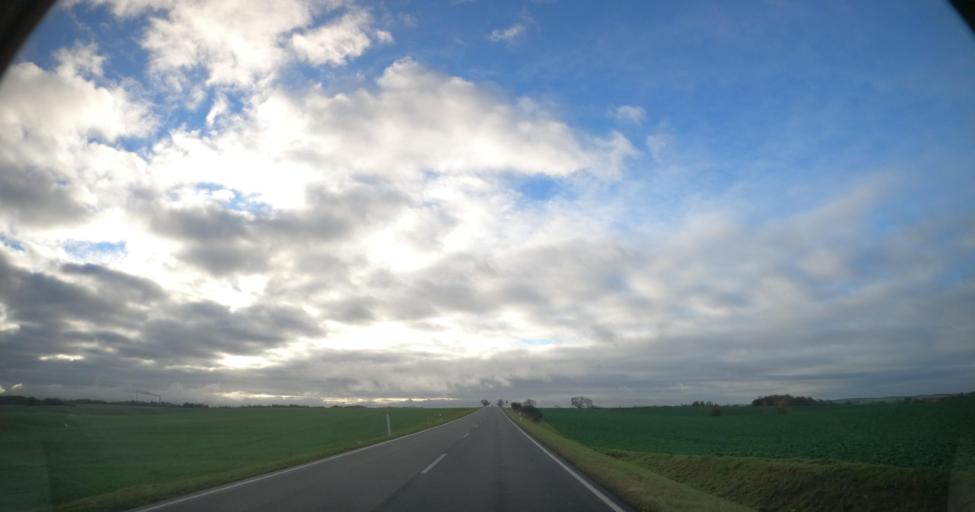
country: DE
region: Brandenburg
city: Mescherin
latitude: 53.2471
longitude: 14.3971
